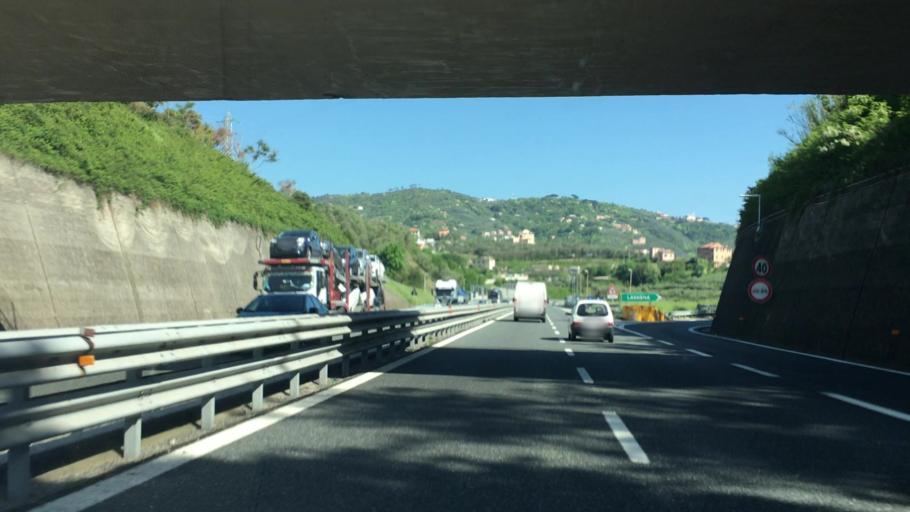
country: IT
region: Liguria
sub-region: Provincia di Genova
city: Lavagna
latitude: 44.3178
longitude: 9.3496
